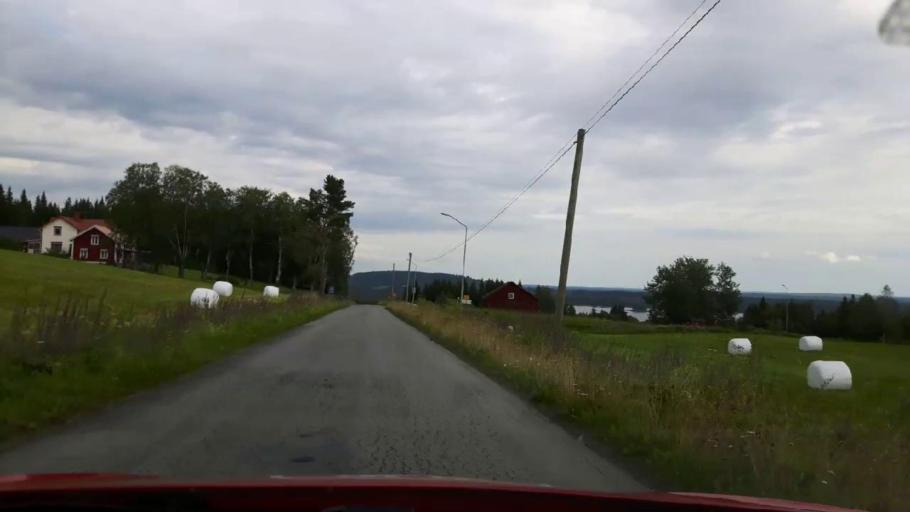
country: SE
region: Jaemtland
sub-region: Stroemsunds Kommun
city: Stroemsund
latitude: 63.5253
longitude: 15.3578
